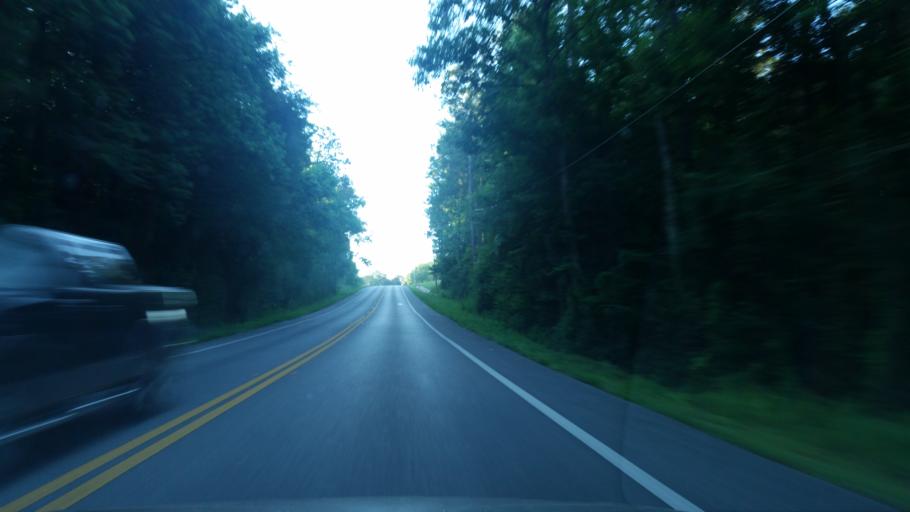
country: US
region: Florida
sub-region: Escambia County
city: Cantonment
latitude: 30.5999
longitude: -87.3542
